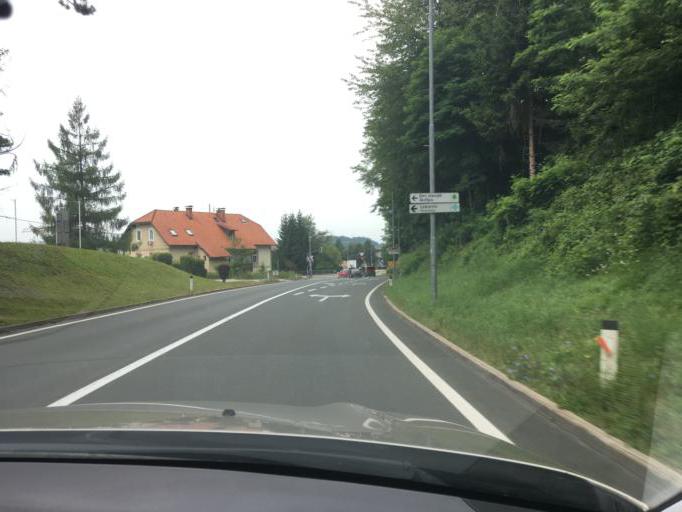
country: SI
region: Skofljica
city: Skofljica
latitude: 45.9838
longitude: 14.5763
